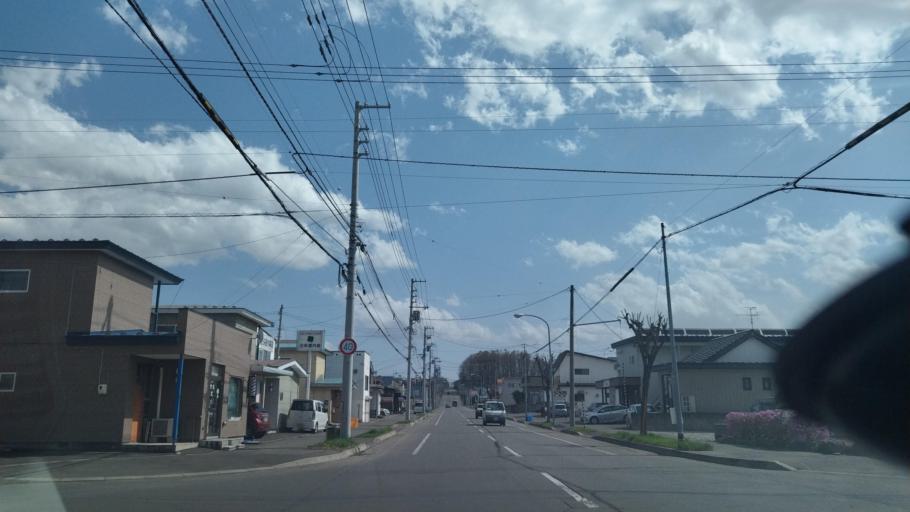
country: JP
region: Hokkaido
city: Obihiro
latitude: 42.9059
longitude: 143.1529
